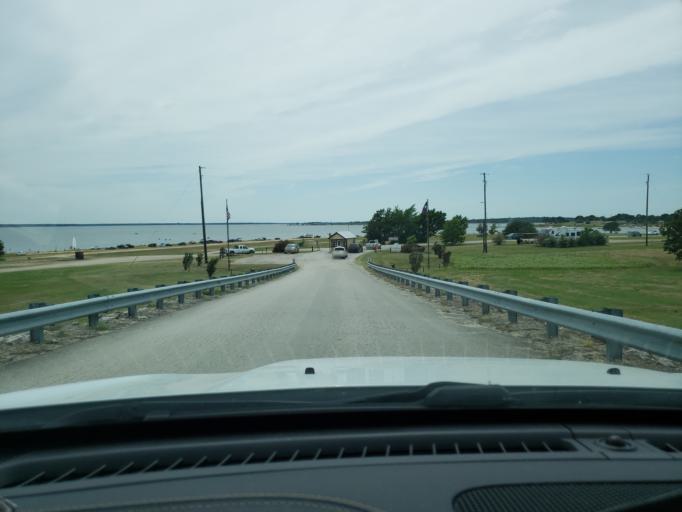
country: US
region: Texas
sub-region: Burleson County
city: Somerville
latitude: 30.3359
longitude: -96.5411
